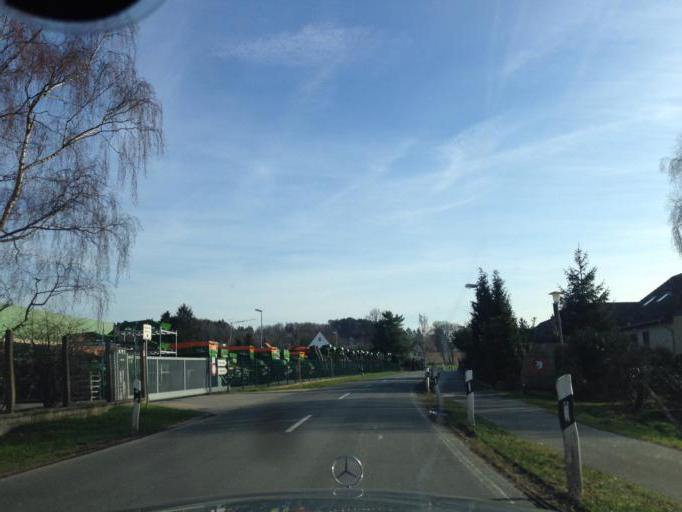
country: DE
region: Lower Saxony
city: Hasbergen
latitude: 52.2190
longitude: 7.8928
